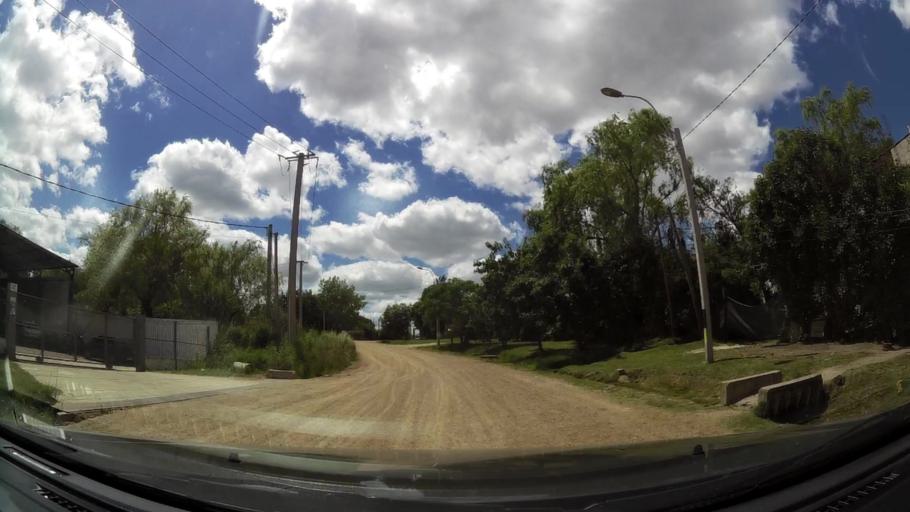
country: UY
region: Canelones
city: Colonia Nicolich
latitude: -34.8165
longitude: -56.0394
